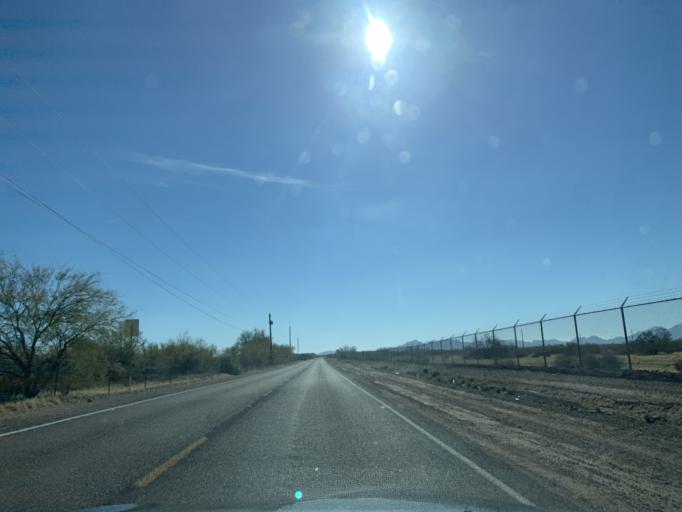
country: US
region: Arizona
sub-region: Maricopa County
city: Queen Creek
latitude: 33.3010
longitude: -111.6049
